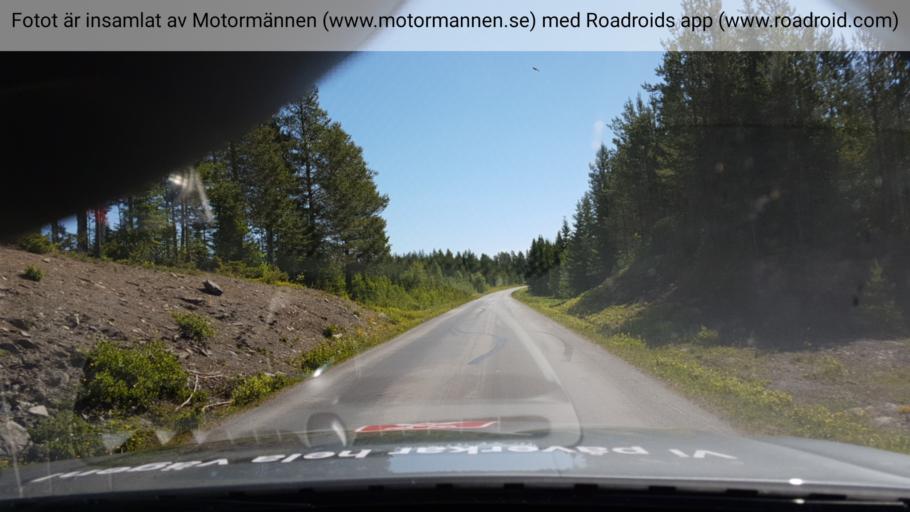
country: SE
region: Jaemtland
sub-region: OEstersunds Kommun
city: Ostersund
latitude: 63.0053
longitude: 14.6264
